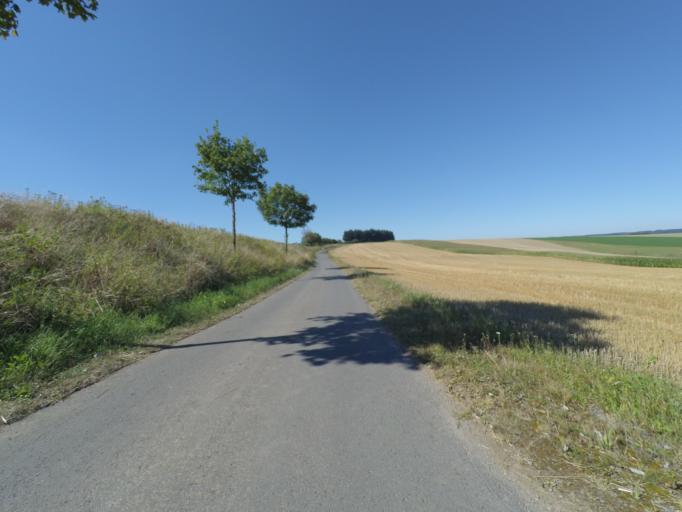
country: DE
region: Rheinland-Pfalz
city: Lutzerath
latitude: 50.1087
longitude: 7.0133
